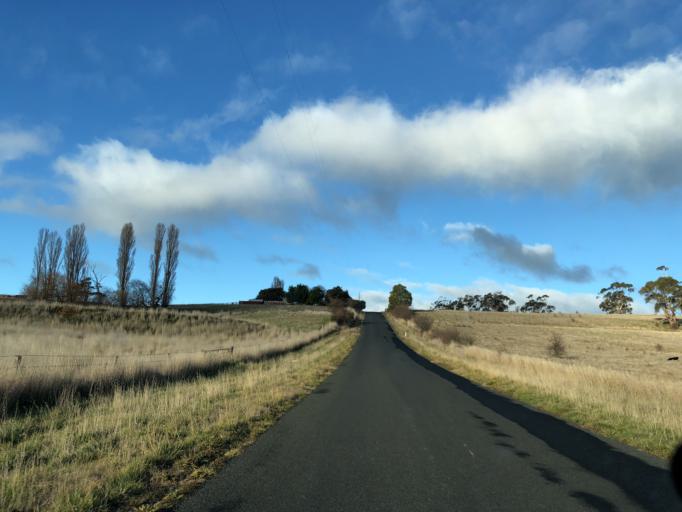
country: AU
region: Victoria
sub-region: Mount Alexander
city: Castlemaine
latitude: -37.2130
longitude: 144.3309
